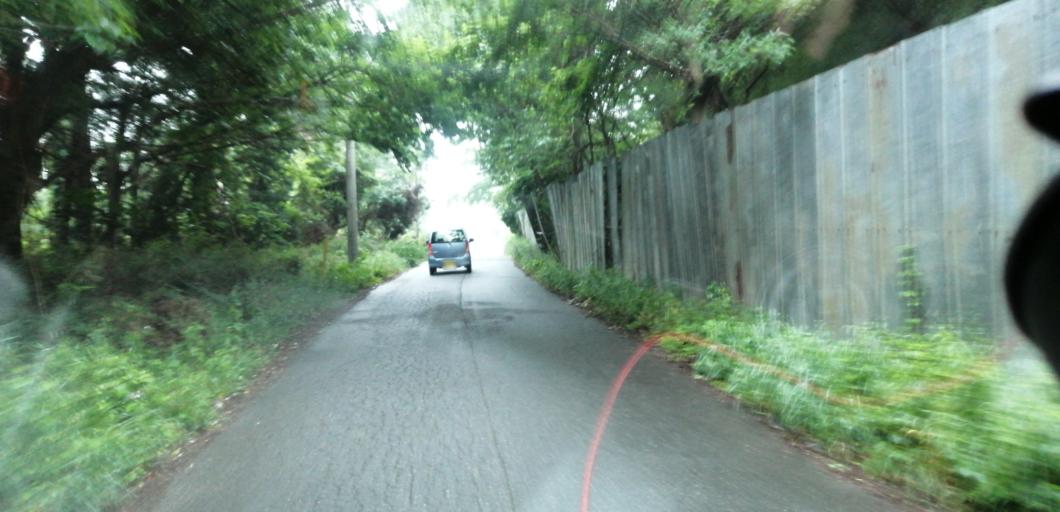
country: JP
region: Chiba
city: Ichihara
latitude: 35.4765
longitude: 140.1501
